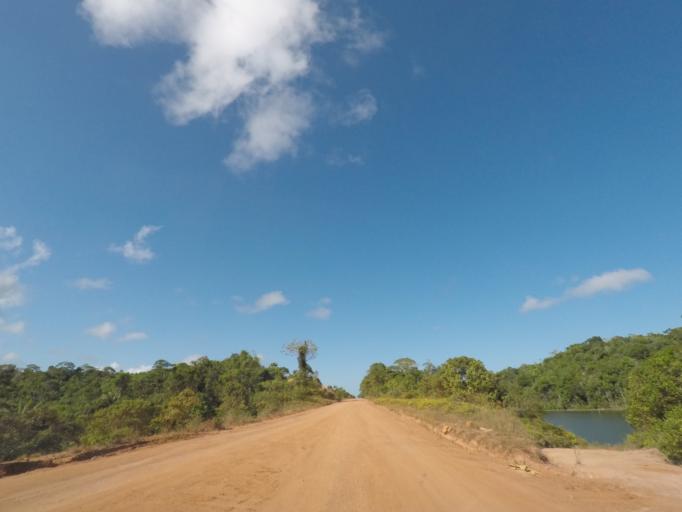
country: BR
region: Bahia
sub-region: Marau
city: Marau
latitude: -14.1321
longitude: -38.9956
